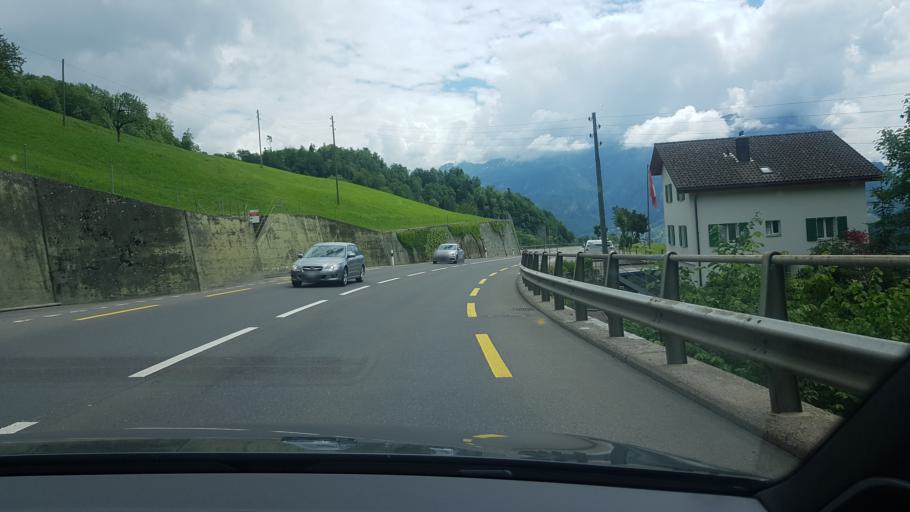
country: CH
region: Schwyz
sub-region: Bezirk Schwyz
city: Steinen
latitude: 47.0540
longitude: 8.6257
